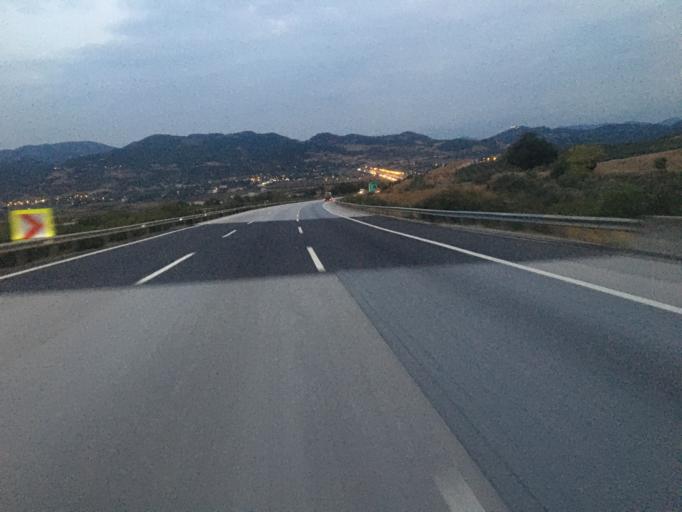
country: TR
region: Osmaniye
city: Haruniye
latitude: 37.2010
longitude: 36.3972
